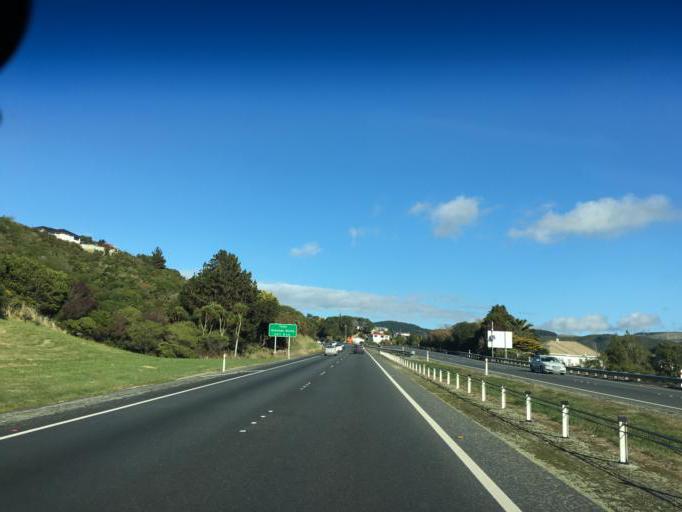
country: NZ
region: Wellington
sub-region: Porirua City
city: Porirua
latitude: -41.1671
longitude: 174.8329
